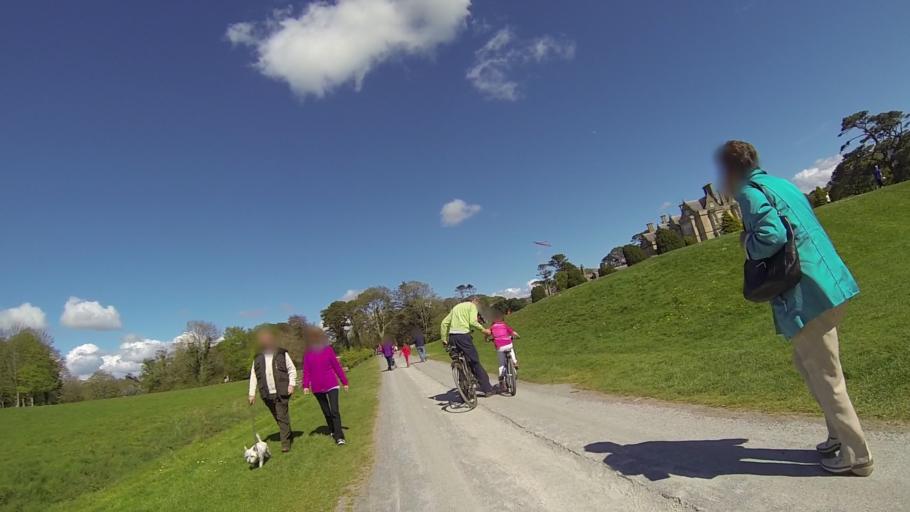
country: IE
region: Munster
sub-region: Ciarrai
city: Cill Airne
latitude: 52.0184
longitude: -9.5058
